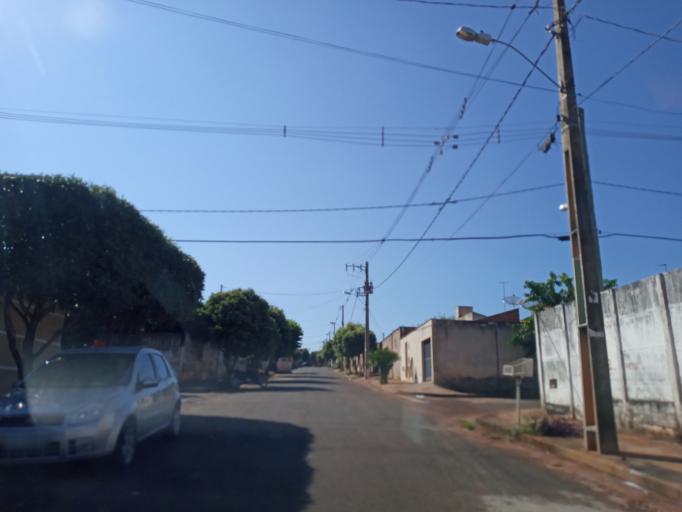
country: BR
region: Minas Gerais
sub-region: Ituiutaba
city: Ituiutaba
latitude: -18.9744
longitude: -49.4890
